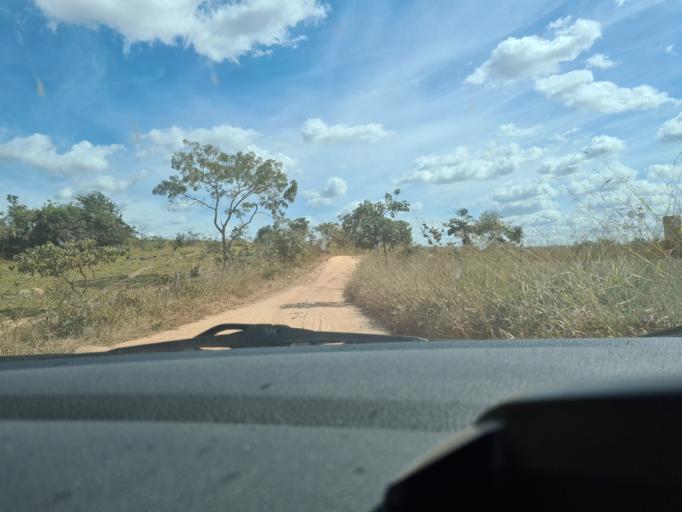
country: BR
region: Goias
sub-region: Silvania
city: Silvania
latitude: -16.5419
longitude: -48.5766
